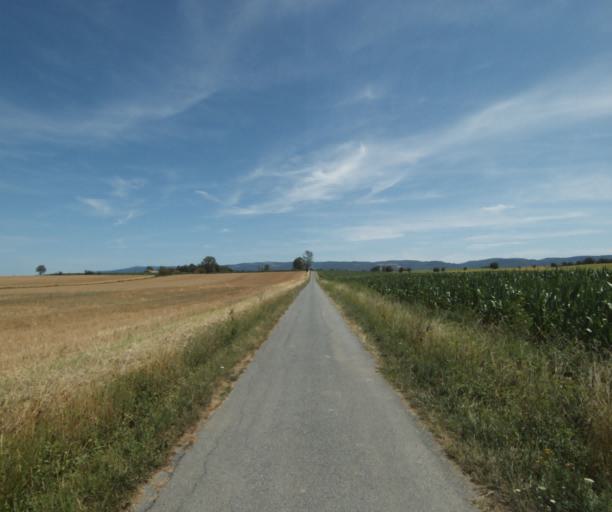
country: FR
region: Midi-Pyrenees
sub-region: Departement de la Haute-Garonne
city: Revel
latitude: 43.5114
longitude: 2.0123
